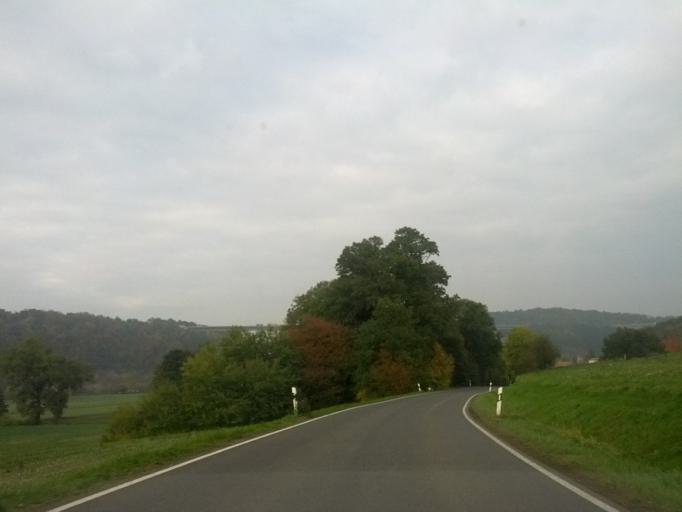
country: DE
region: Thuringia
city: Krauthausen
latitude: 51.0035
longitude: 10.2185
